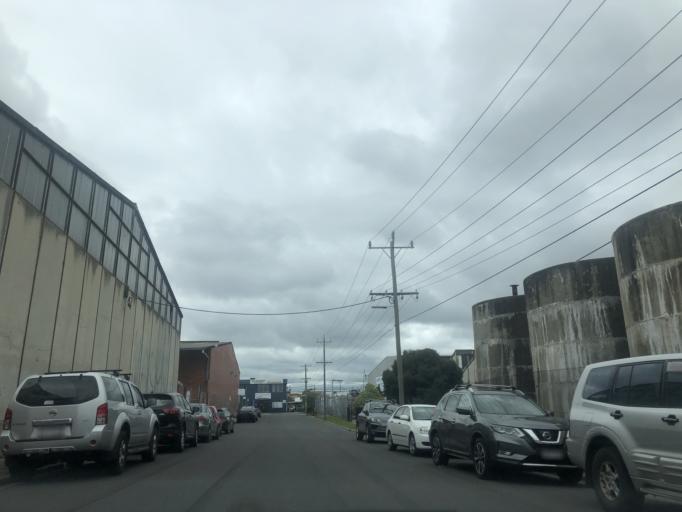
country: AU
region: Victoria
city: Clayton
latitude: -37.9174
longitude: 145.1079
